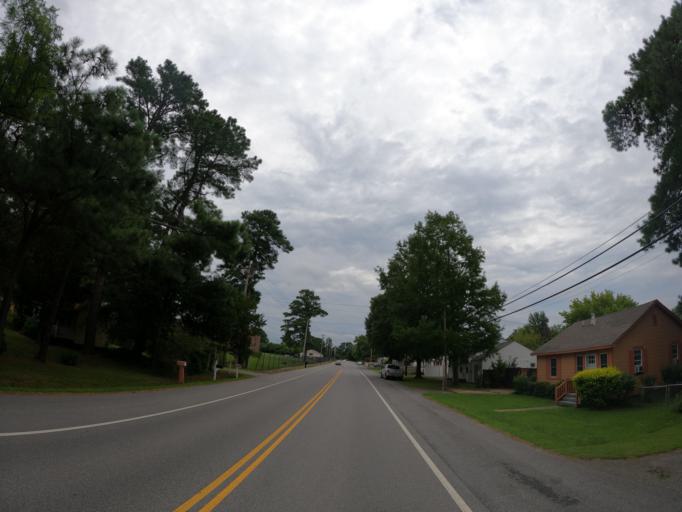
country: US
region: Maryland
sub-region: Saint Mary's County
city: Lexington Park
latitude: 38.1433
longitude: -76.5088
